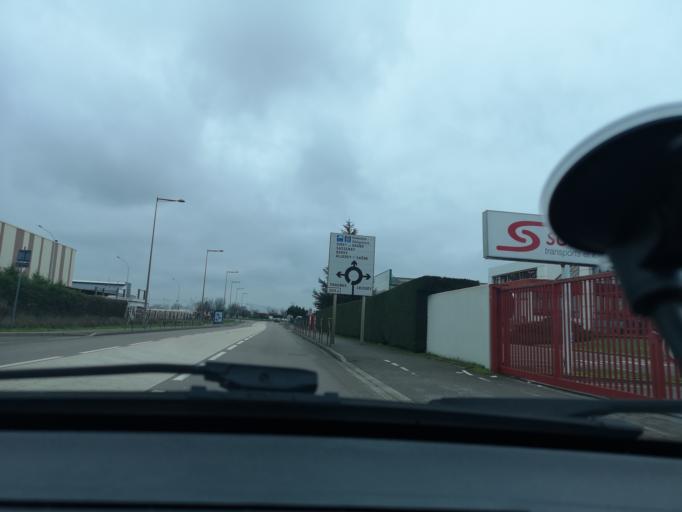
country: FR
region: Bourgogne
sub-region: Departement de Saone-et-Loire
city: Virey-le-Grand
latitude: 46.8220
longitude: 4.8634
